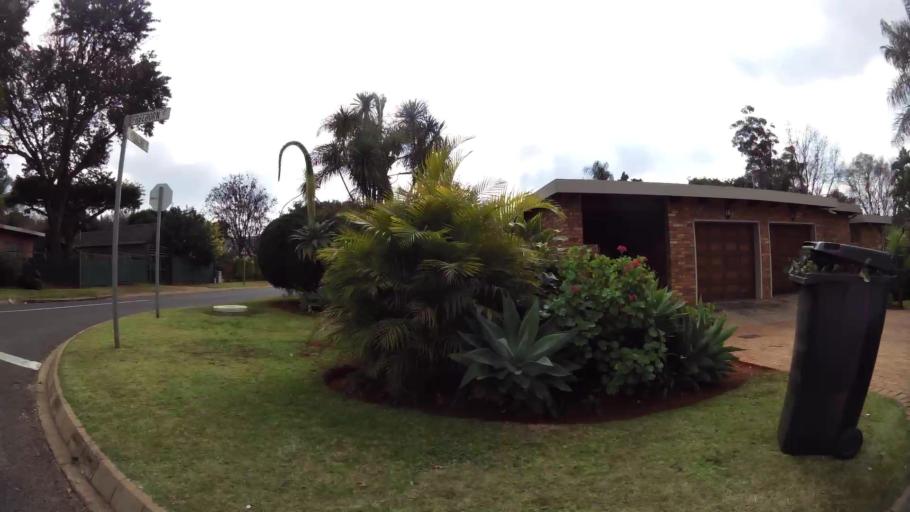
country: ZA
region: Gauteng
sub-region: City of Tshwane Metropolitan Municipality
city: Pretoria
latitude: -25.7592
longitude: 28.3039
